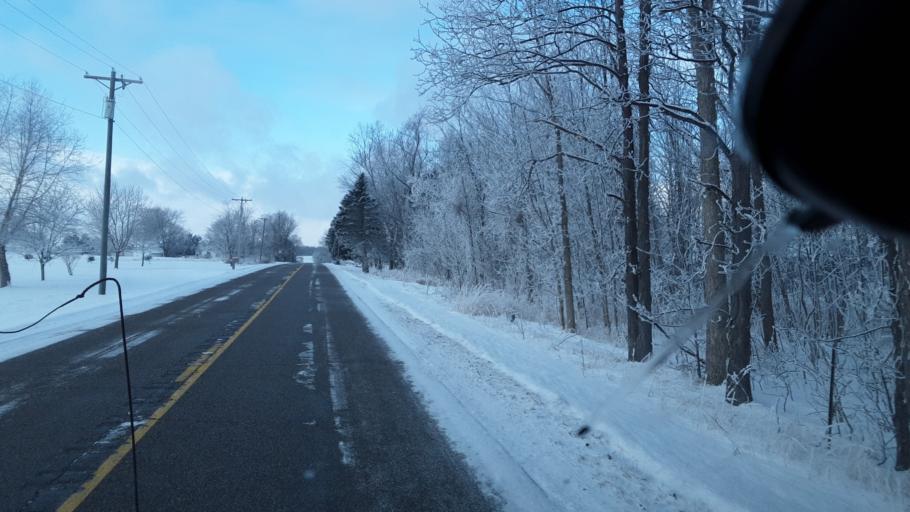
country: US
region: Michigan
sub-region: Eaton County
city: Eaton Rapids
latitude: 42.4875
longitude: -84.6109
